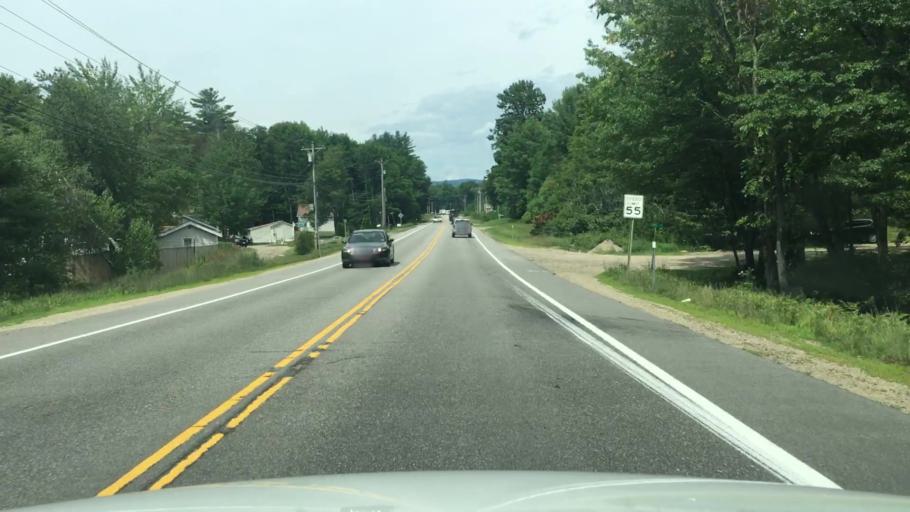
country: US
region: New Hampshire
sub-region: Grafton County
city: Ashland
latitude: 43.6210
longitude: -71.5949
